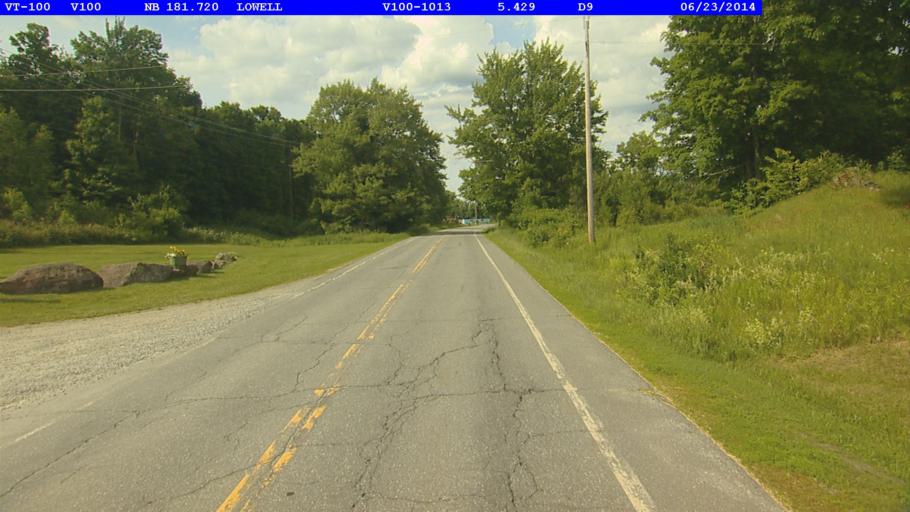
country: US
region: Vermont
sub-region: Orleans County
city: Newport
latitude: 44.8137
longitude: -72.4434
